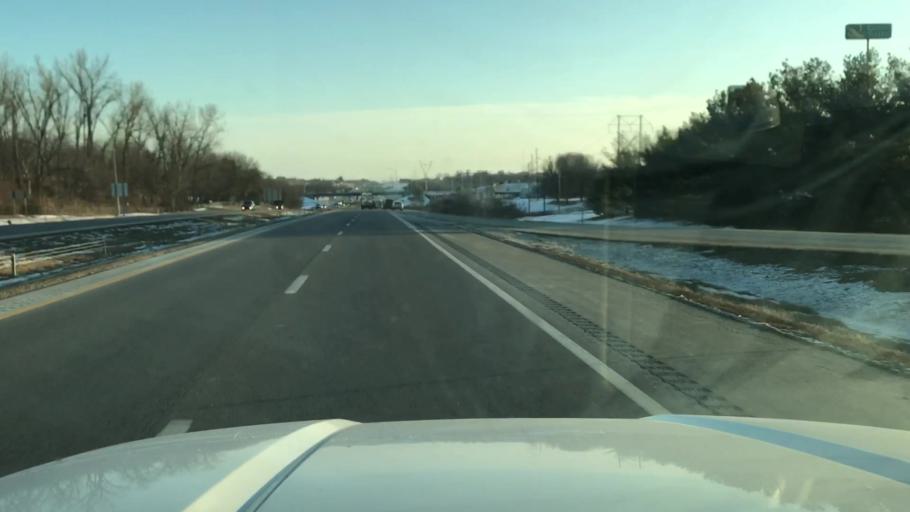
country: US
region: Missouri
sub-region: Buchanan County
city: Saint Joseph
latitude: 39.7756
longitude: -94.7937
